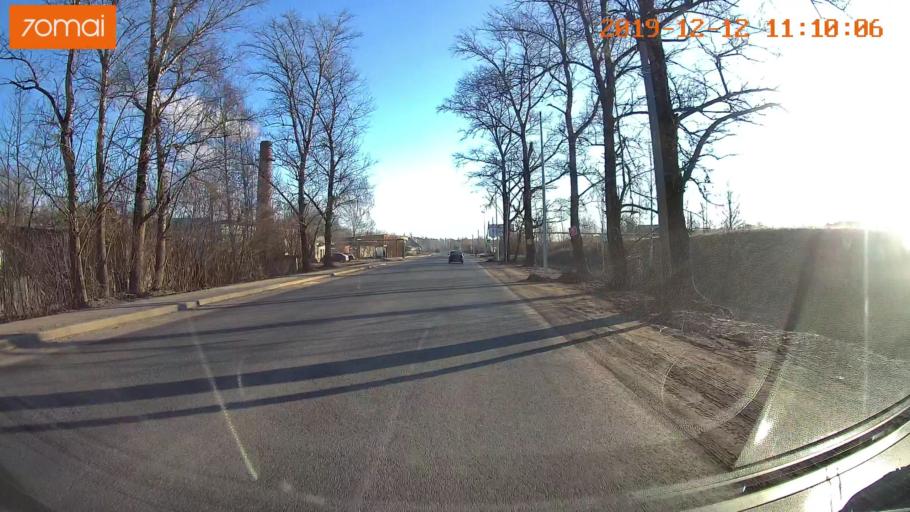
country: RU
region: Ivanovo
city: Kokhma
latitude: 56.9268
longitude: 41.0956
